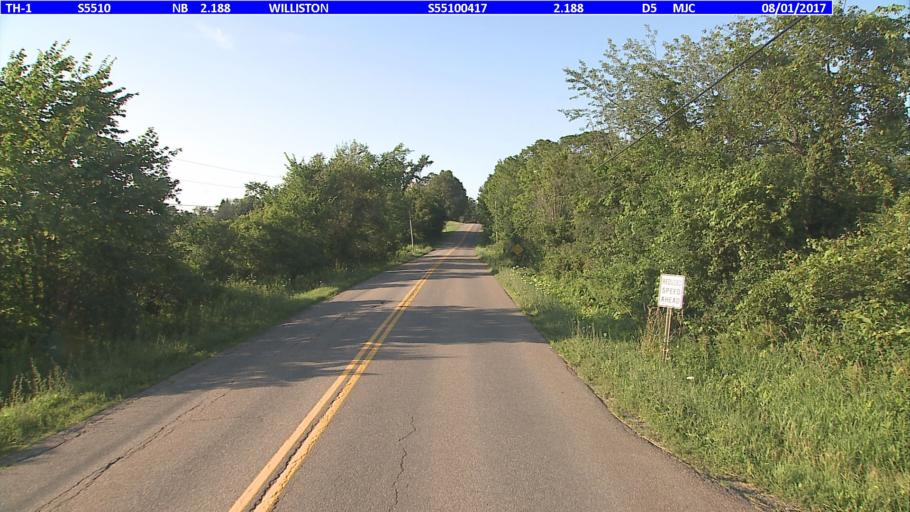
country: US
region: Vermont
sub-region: Chittenden County
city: Williston
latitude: 44.4033
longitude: -73.0907
